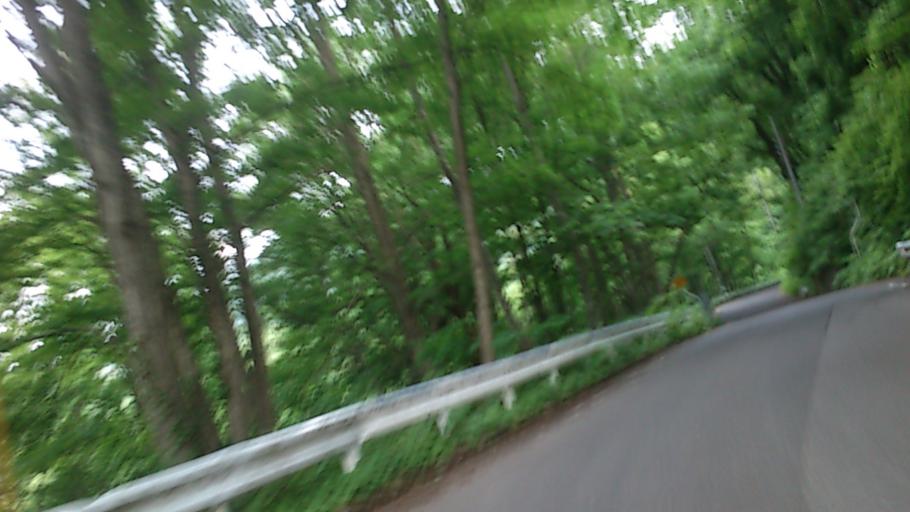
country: JP
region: Aomori
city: Hirosaki
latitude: 40.5197
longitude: 140.1778
